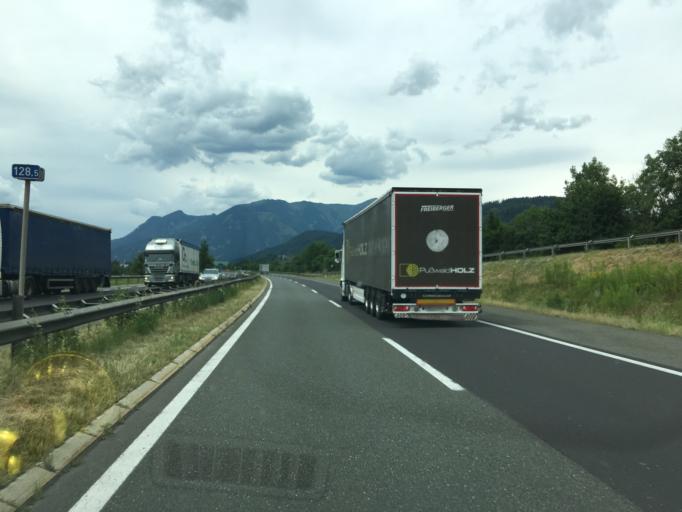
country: AT
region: Styria
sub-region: Politischer Bezirk Leoben
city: Traboch
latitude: 47.3701
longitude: 14.9913
